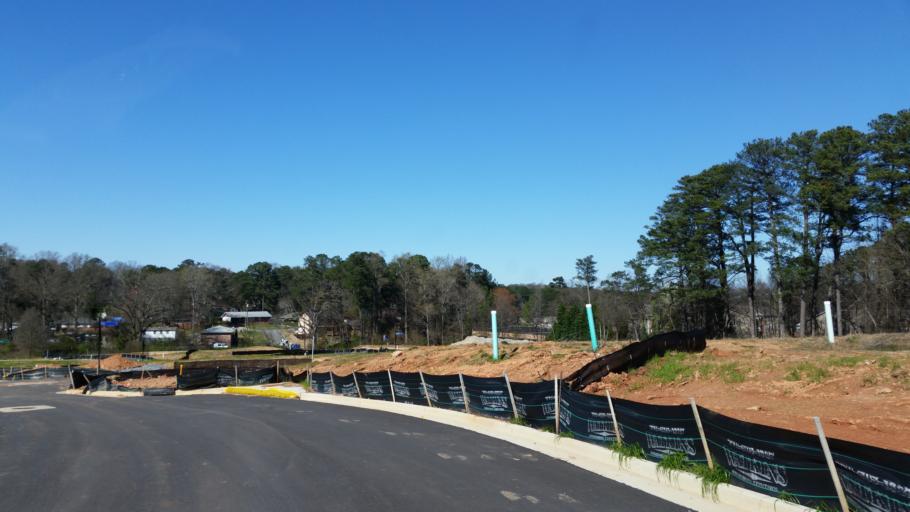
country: US
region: Georgia
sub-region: Cobb County
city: Marietta
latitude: 33.9528
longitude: -84.5266
